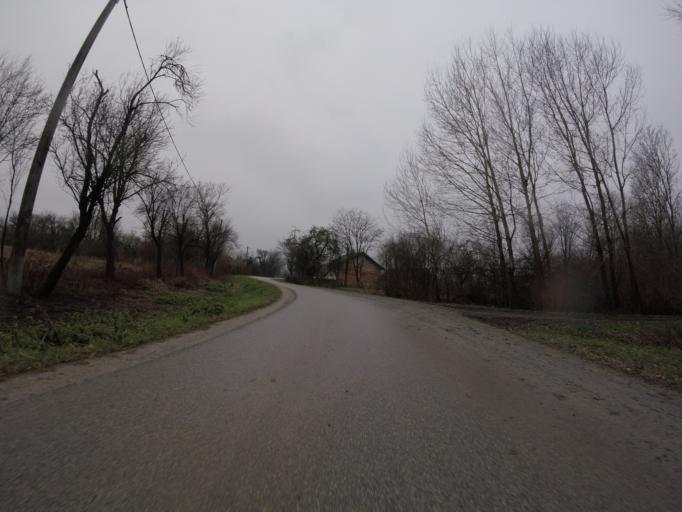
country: HR
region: Sisacko-Moslavacka
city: Lekenik
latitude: 45.6332
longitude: 16.3104
